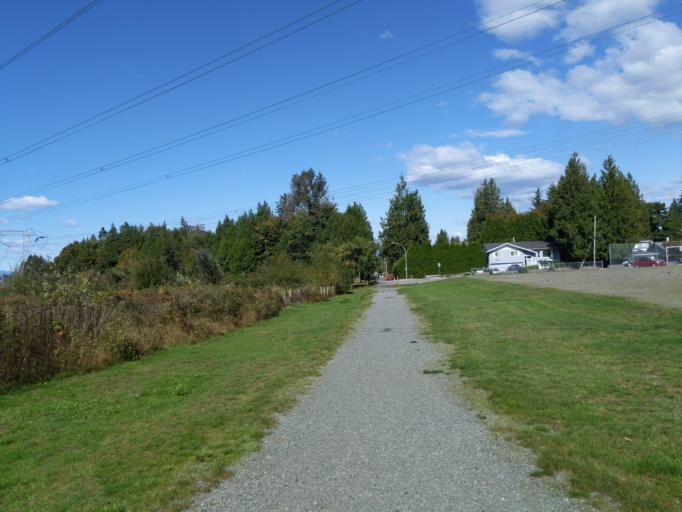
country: CA
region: British Columbia
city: Langley
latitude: 49.0887
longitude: -122.6795
